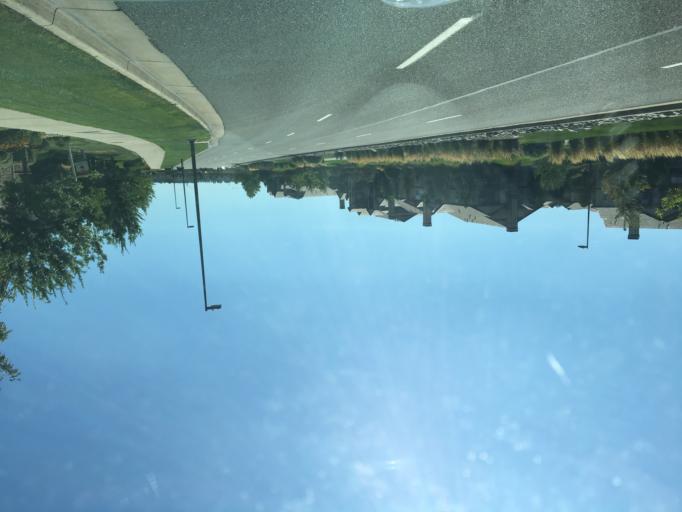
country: US
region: Colorado
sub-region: Douglas County
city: Parker
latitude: 39.5936
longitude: -104.7231
